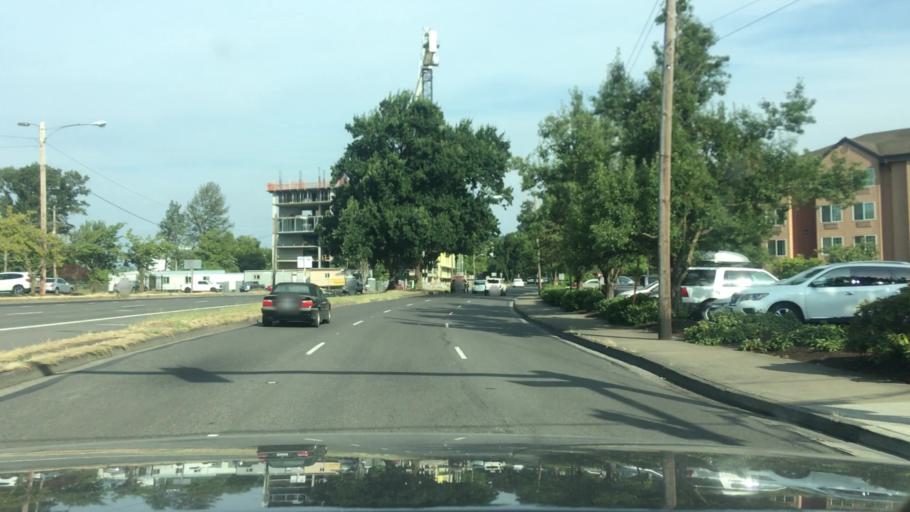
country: US
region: Oregon
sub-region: Lane County
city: Eugene
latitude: 44.0496
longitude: -123.0801
